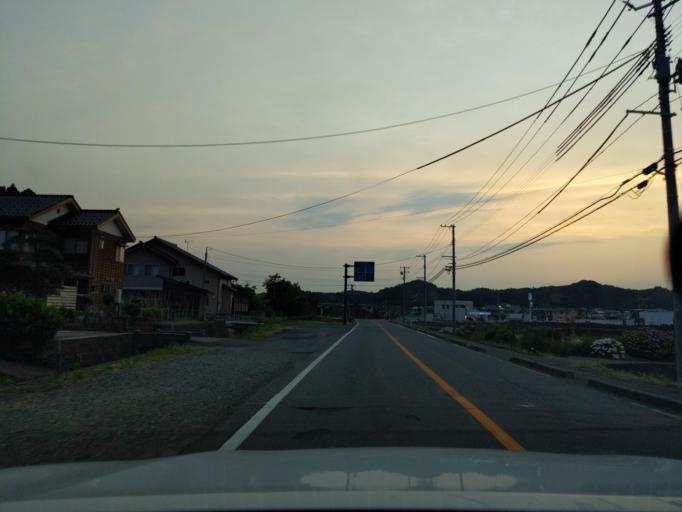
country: JP
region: Niigata
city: Kashiwazaki
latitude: 37.4463
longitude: 138.6435
